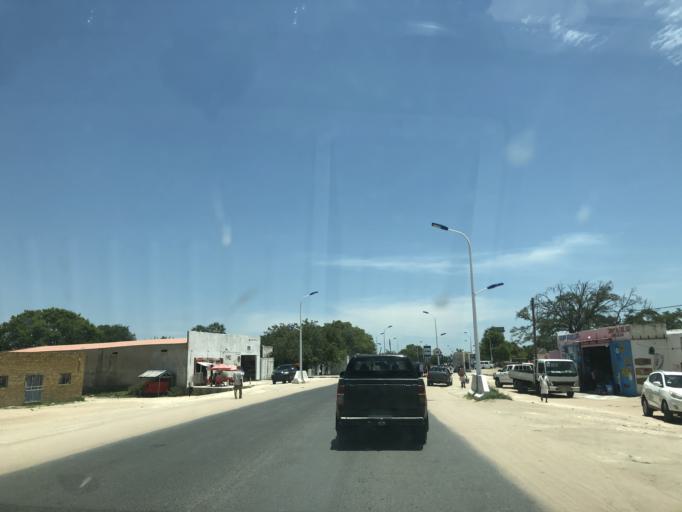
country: AO
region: Cunene
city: Ondjiva
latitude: -17.0742
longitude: 15.7334
